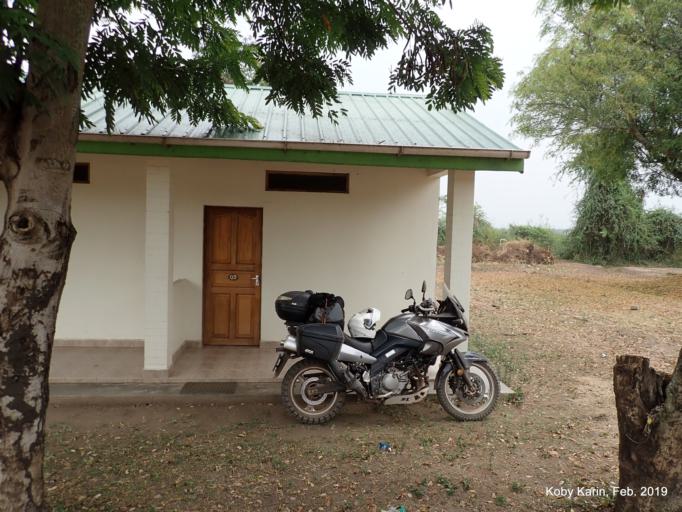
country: UG
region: Western Region
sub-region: Rubirizi District
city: Rubirizi
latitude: -0.1936
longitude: 29.9008
